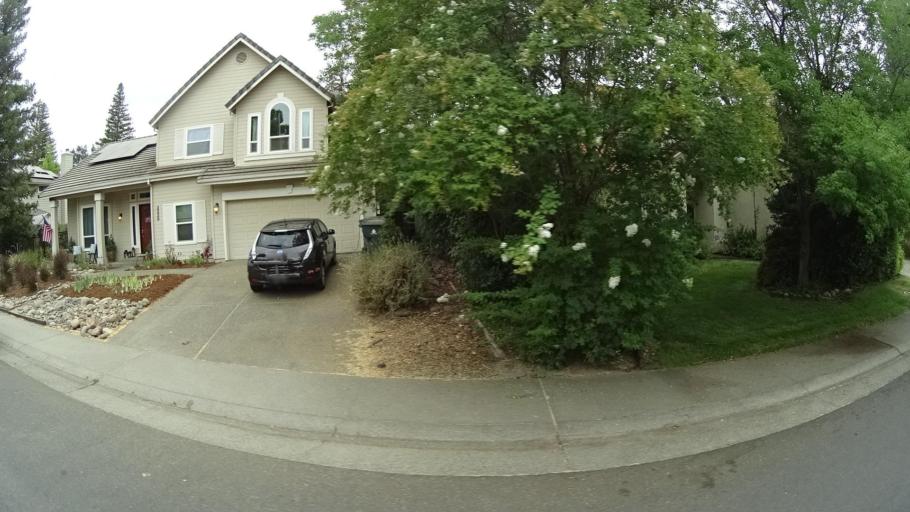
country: US
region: California
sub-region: Placer County
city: Rocklin
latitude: 38.7956
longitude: -121.2589
